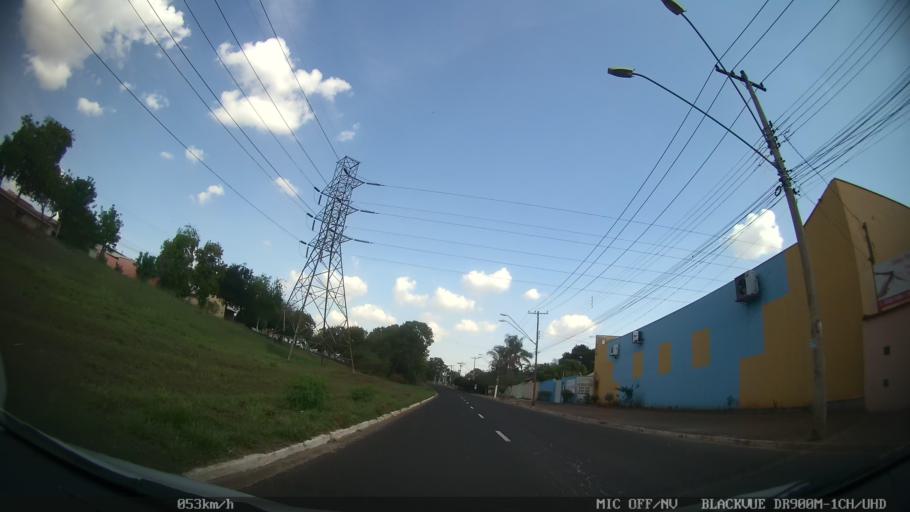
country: BR
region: Sao Paulo
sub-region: Ribeirao Preto
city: Ribeirao Preto
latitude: -21.1814
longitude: -47.8408
